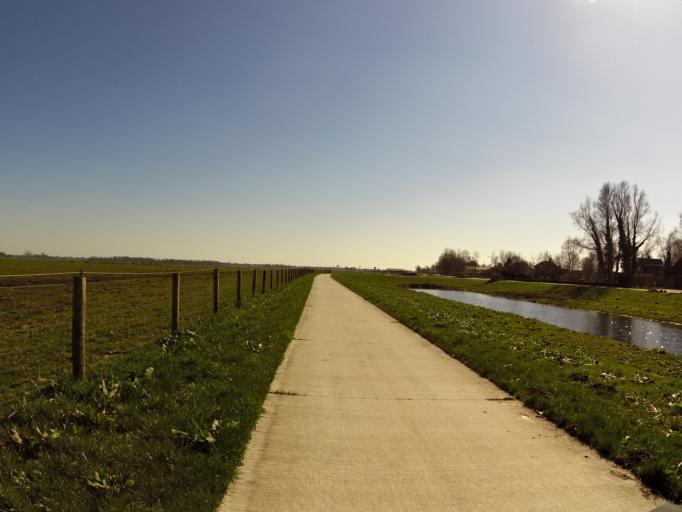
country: NL
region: Overijssel
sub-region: Gemeente Steenwijkerland
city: Blokzijl
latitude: 52.7690
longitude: 5.9897
